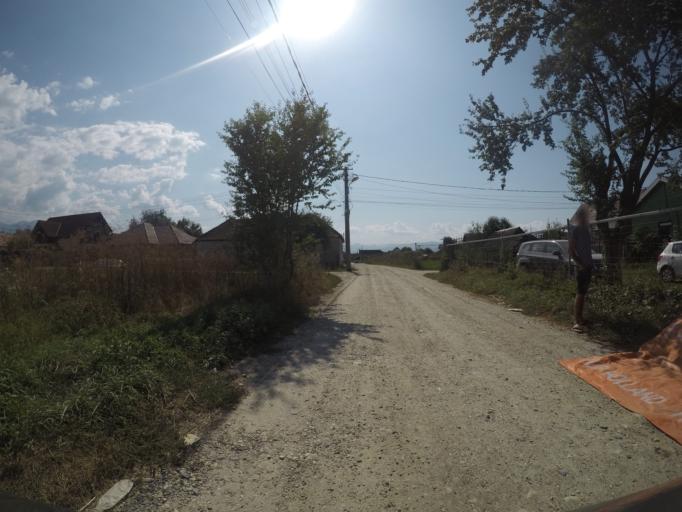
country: RO
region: Sibiu
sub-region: Comuna Avrig
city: Avrig
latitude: 45.7280
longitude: 24.3877
